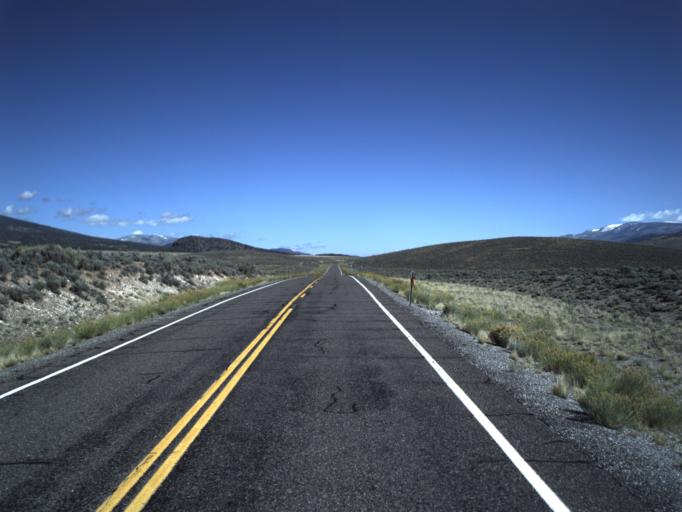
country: US
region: Utah
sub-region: Piute County
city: Junction
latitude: 38.3077
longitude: -111.9688
